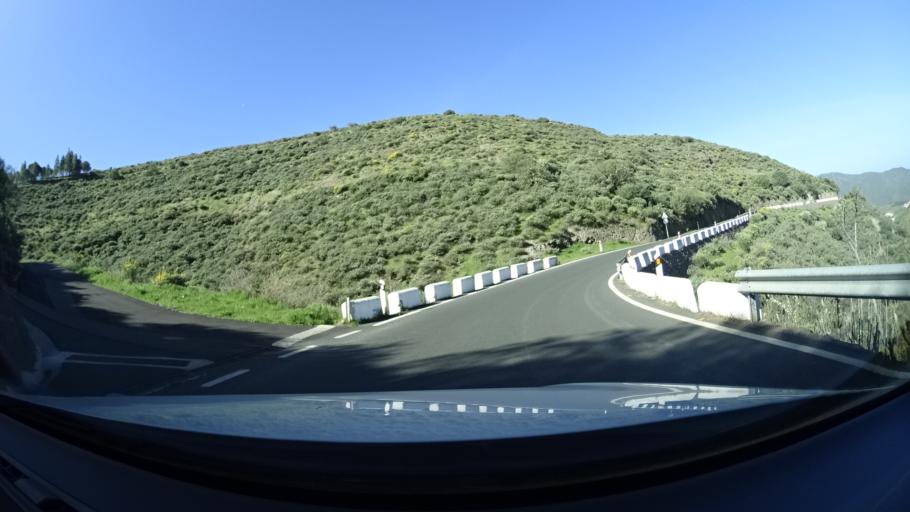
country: ES
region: Canary Islands
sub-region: Provincia de Las Palmas
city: Artenara
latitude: 28.0211
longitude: -15.6427
